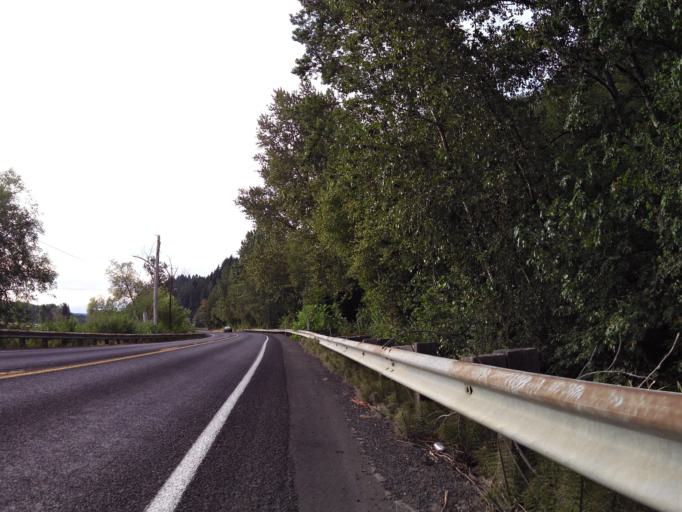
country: US
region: Washington
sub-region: Cowlitz County
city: West Longview
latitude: 46.1869
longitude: -123.0861
